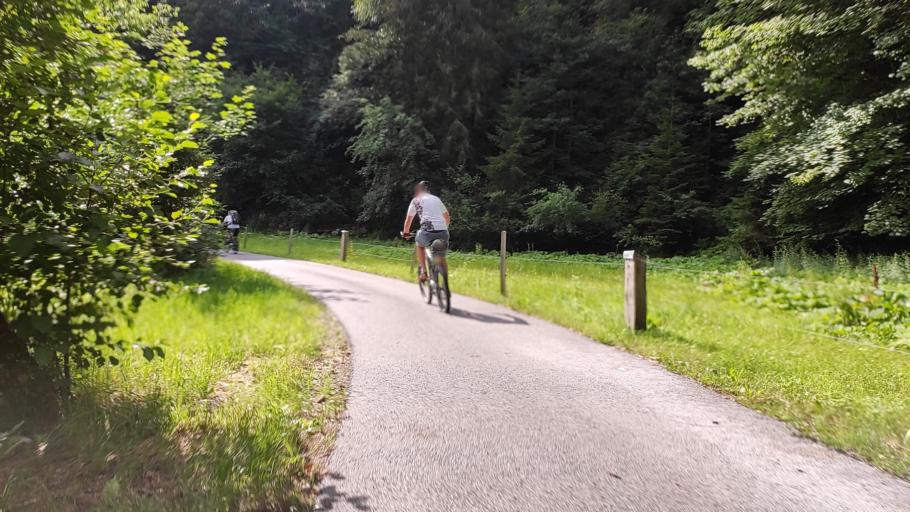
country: AT
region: Salzburg
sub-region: Politischer Bezirk Zell am See
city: Viehhofen
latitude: 47.3629
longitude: 12.7547
